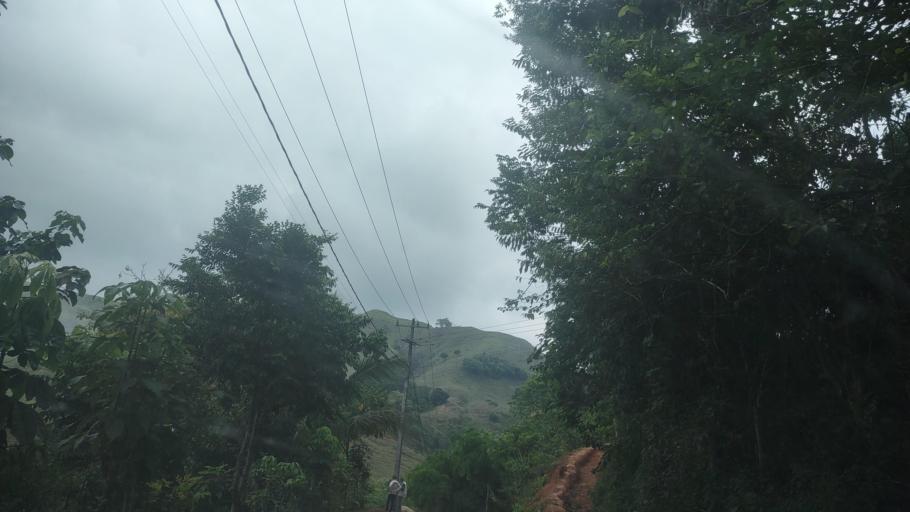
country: MX
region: Tabasco
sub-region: Huimanguillo
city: Francisco Rueda
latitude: 17.4445
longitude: -94.0246
